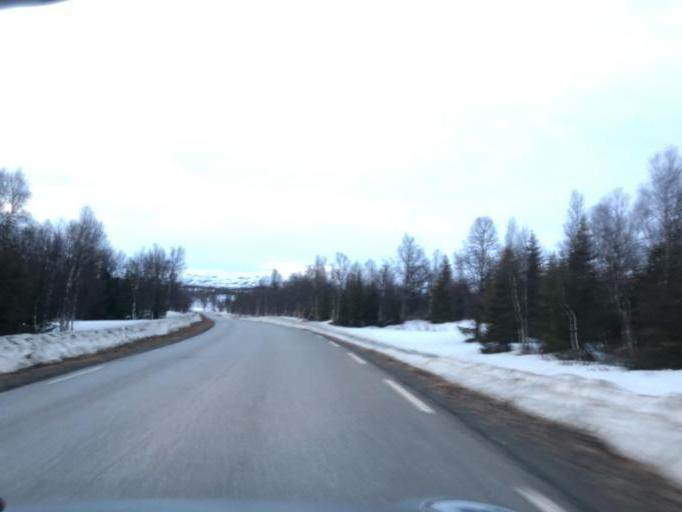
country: NO
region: Sor-Trondelag
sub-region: Tydal
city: Aas
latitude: 62.7203
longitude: 11.8230
